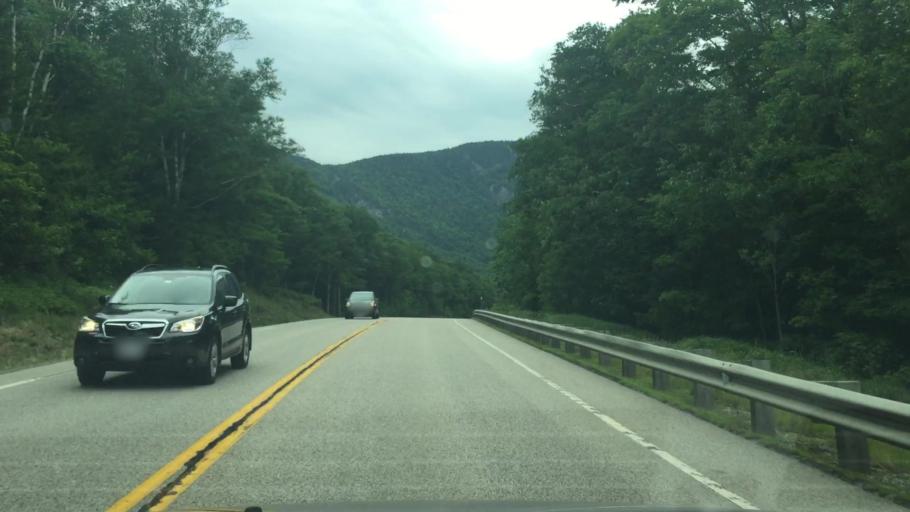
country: US
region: New Hampshire
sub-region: Grafton County
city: Deerfield
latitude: 44.1853
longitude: -71.4009
